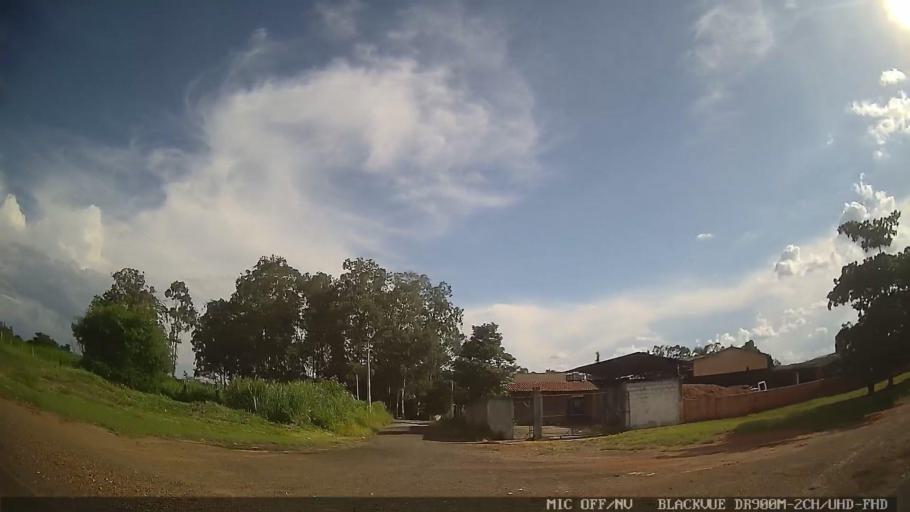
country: BR
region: Sao Paulo
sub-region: Laranjal Paulista
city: Laranjal Paulista
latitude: -23.0779
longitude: -47.8022
